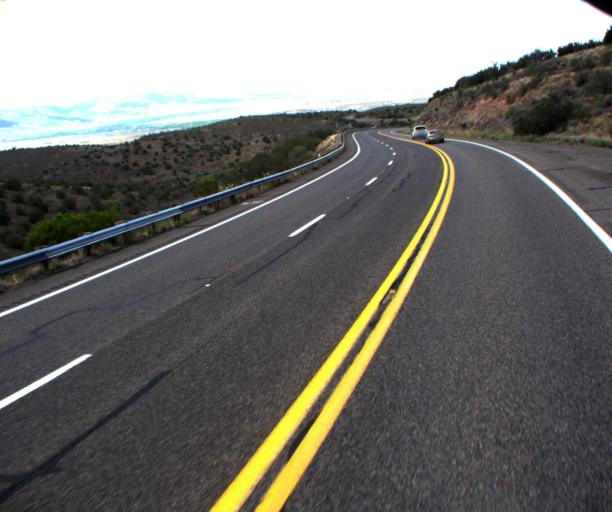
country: US
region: Arizona
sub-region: Yavapai County
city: Lake Montezuma
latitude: 34.5003
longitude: -111.7198
